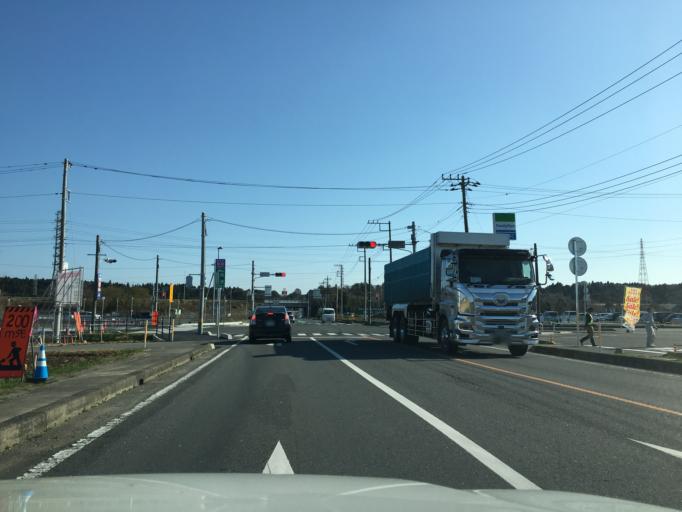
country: JP
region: Ibaraki
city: Mito-shi
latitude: 36.4192
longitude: 140.4239
